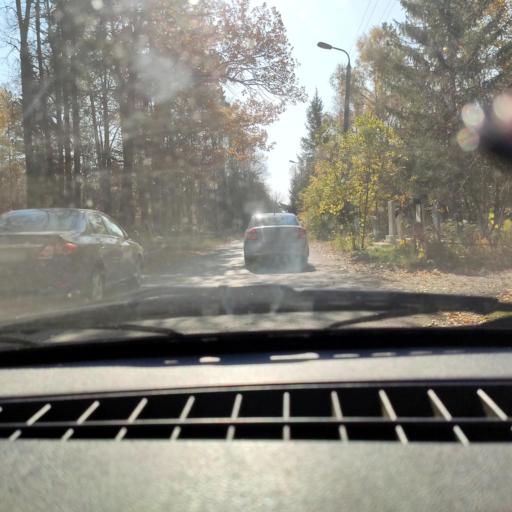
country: RU
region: Bashkortostan
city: Mikhaylovka
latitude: 54.8103
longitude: 55.8630
